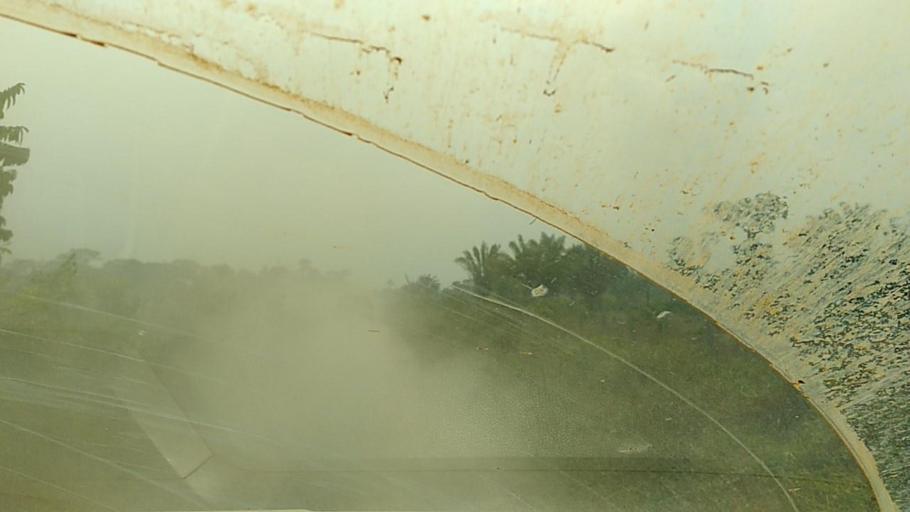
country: BR
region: Rondonia
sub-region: Porto Velho
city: Porto Velho
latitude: -8.7722
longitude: -63.1760
